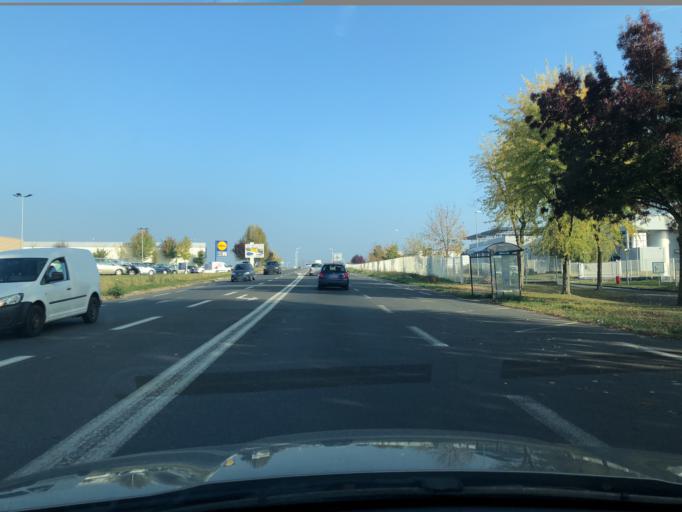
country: FR
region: Centre
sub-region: Departement d'Indre-et-Loire
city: Chanceaux-sur-Choisille
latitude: 47.4390
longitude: 0.6994
